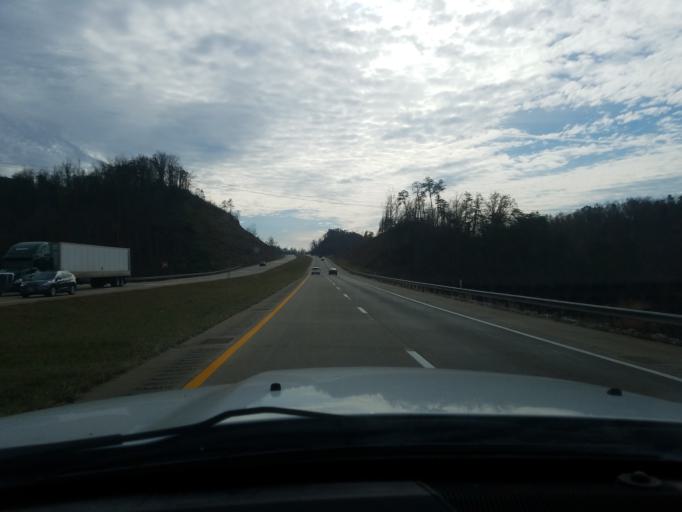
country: US
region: West Virginia
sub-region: Putnam County
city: Eleanor
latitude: 38.5128
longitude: -81.9322
